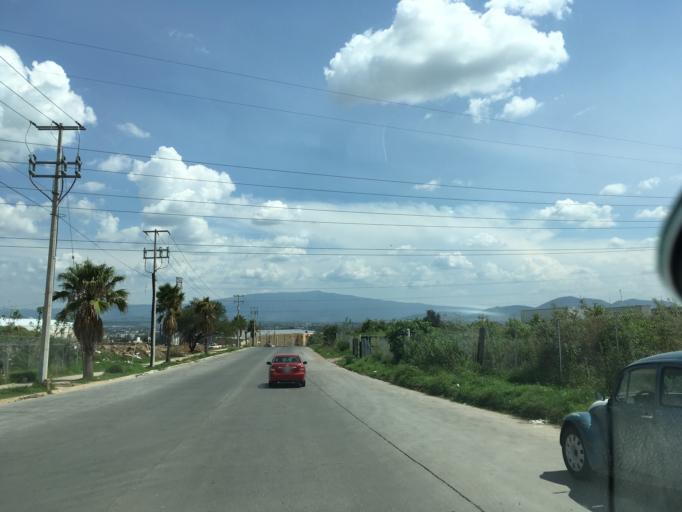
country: MX
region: Jalisco
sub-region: Tlajomulco de Zuniga
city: Altus Bosques
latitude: 20.5865
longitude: -103.3589
